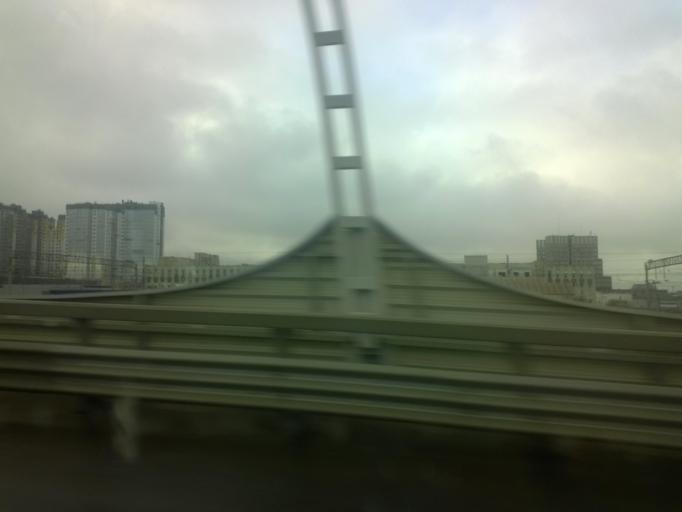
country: RU
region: St.-Petersburg
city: Avtovo
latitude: 59.8532
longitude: 30.2902
